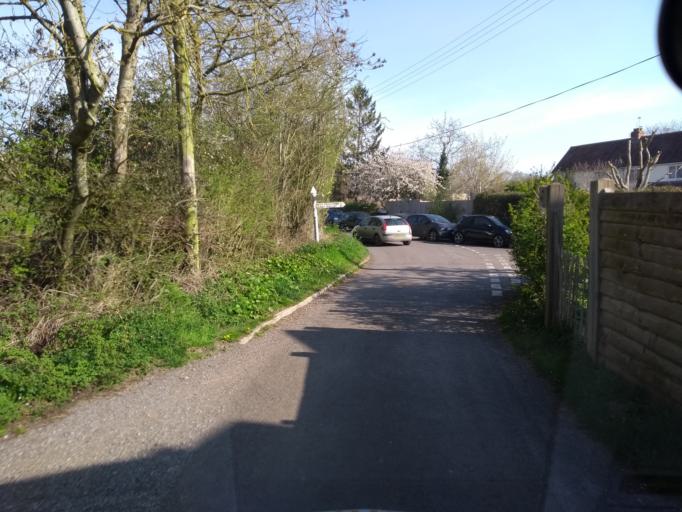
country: GB
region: England
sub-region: Somerset
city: Creech Saint Michael
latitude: 50.9759
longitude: -2.9906
